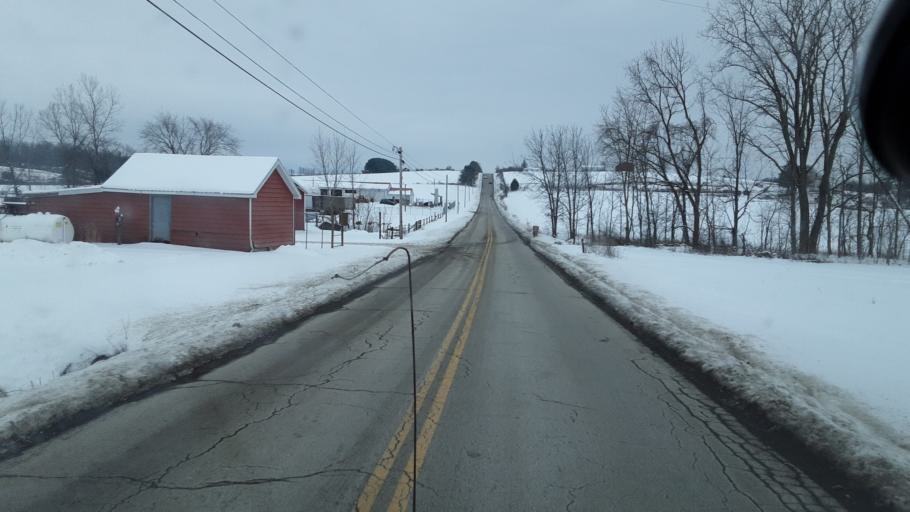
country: US
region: Ohio
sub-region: Perry County
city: Somerset
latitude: 39.9356
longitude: -82.2235
